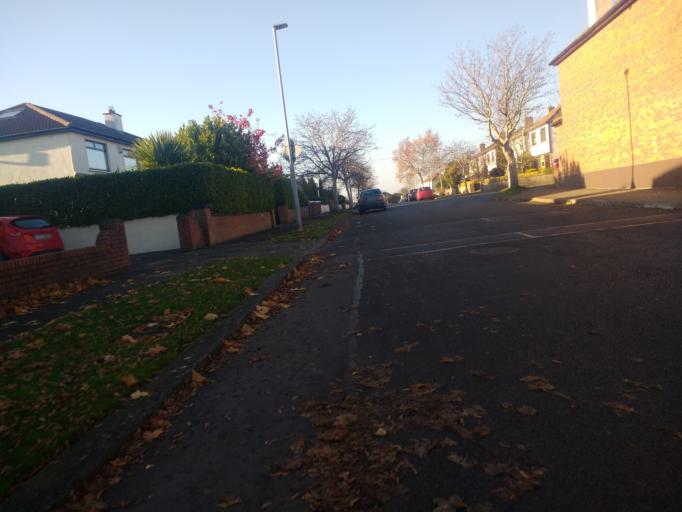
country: IE
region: Leinster
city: Kinsealy-Drinan
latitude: 53.4530
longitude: -6.1859
